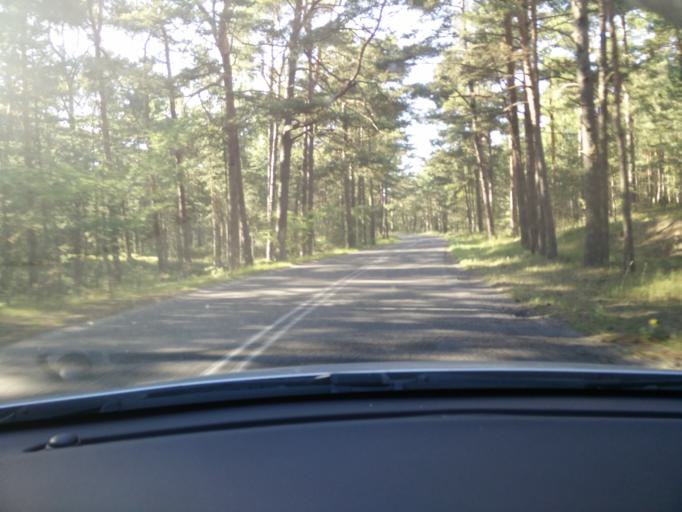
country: PL
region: Pomeranian Voivodeship
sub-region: Powiat pucki
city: Hel
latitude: 54.6399
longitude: 18.7746
